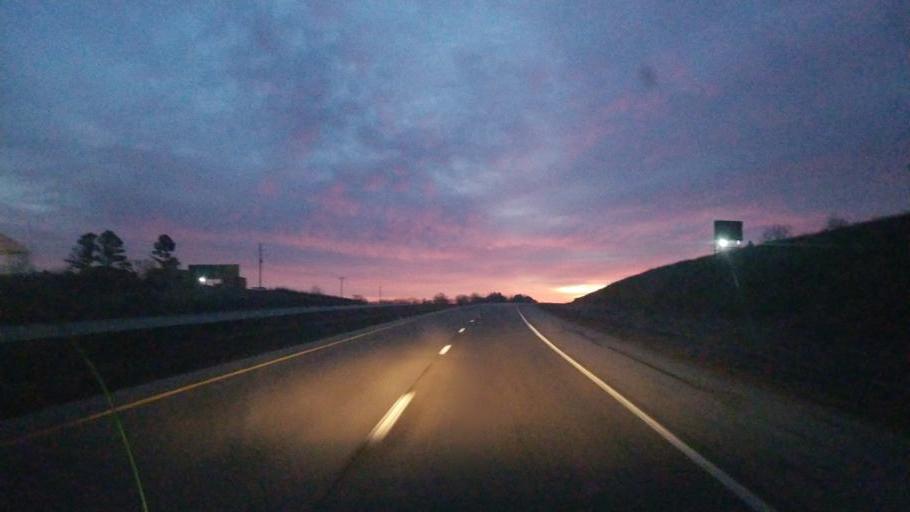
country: US
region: Missouri
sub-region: Shannon County
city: Winona
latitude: 36.9991
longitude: -91.4700
